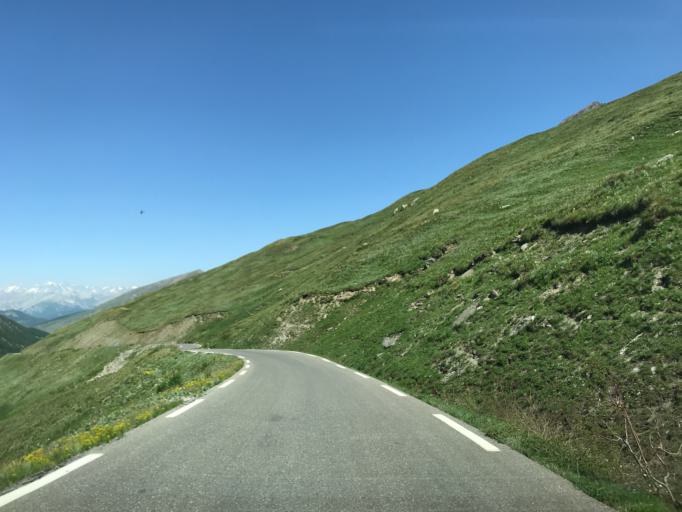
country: IT
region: Piedmont
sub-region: Provincia di Cuneo
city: Pontechianale
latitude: 44.6953
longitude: 6.9571
